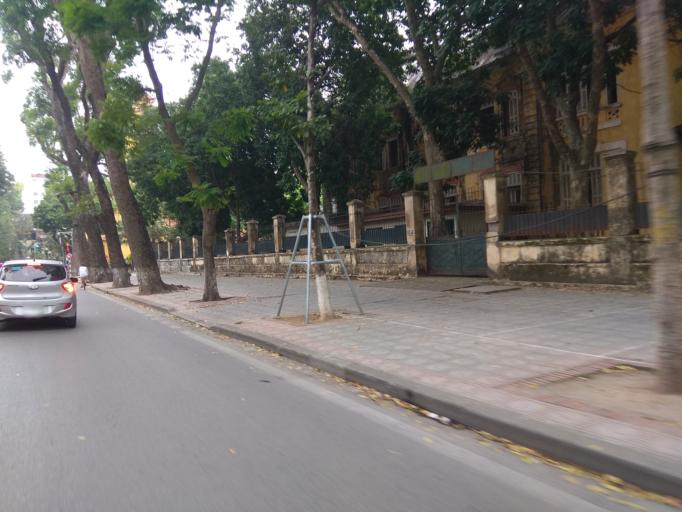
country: VN
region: Ha Noi
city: Hanoi
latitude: 21.0402
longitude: 105.8400
